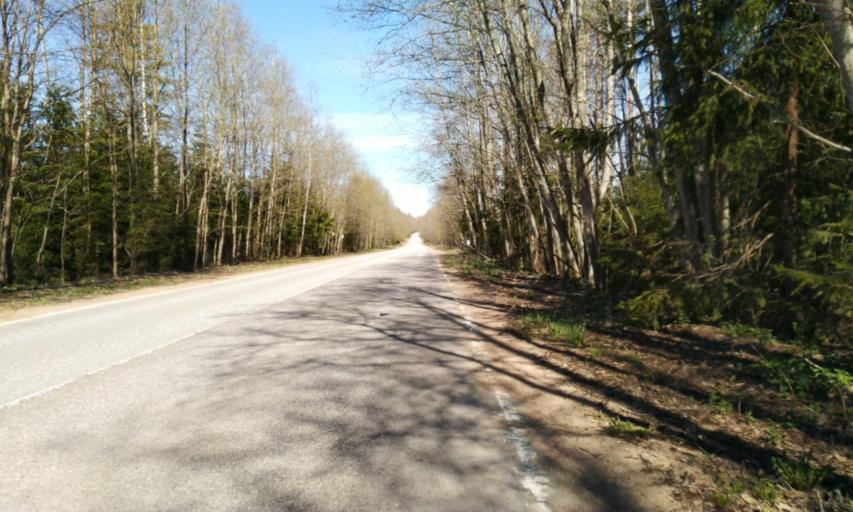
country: RU
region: Leningrad
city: Garbolovo
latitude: 60.4034
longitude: 30.4723
